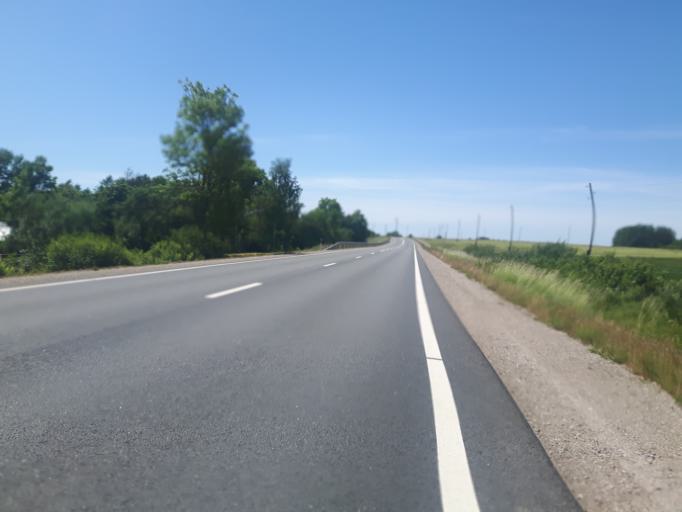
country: LV
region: Durbe
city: Liegi
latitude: 56.5632
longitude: 21.2675
